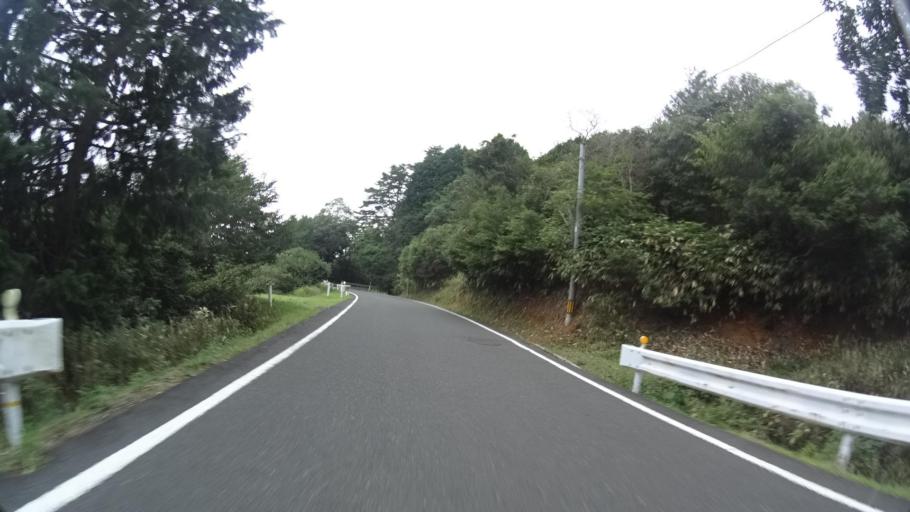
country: JP
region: Kyoto
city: Miyazu
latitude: 35.4743
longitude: 135.1582
